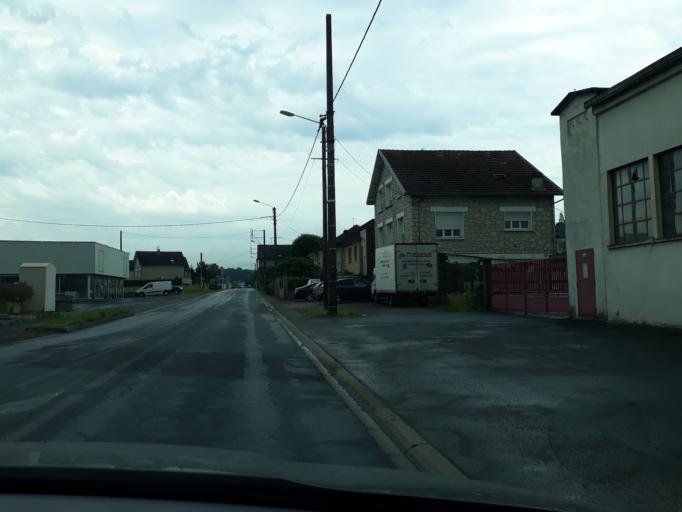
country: FR
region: Limousin
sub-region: Departement de la Correze
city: Malemort-sur-Correze
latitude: 45.1600
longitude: 1.5685
